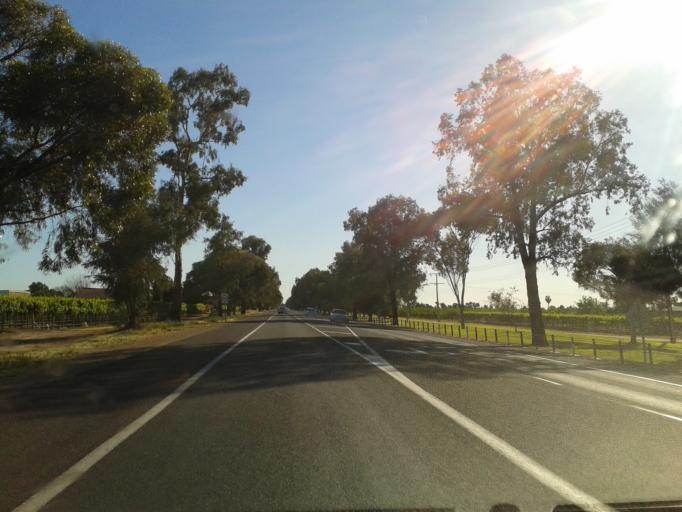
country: AU
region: South Australia
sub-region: Renmark Paringa
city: Renmark West
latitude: -34.2008
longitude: 140.7110
